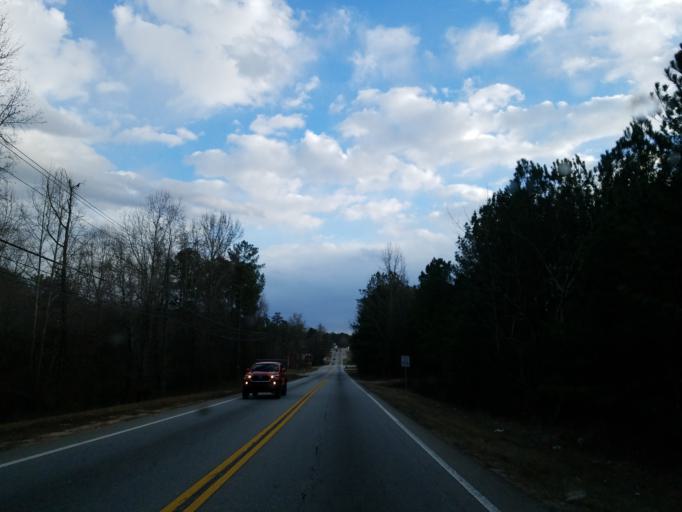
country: US
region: Georgia
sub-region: Henry County
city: Stockbridge
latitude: 33.5382
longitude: -84.2013
